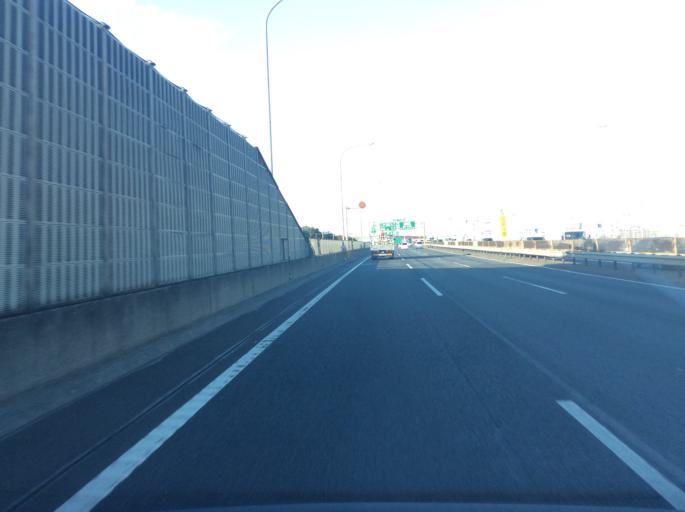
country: JP
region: Saitama
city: Yashio-shi
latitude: 35.8415
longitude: 139.8677
